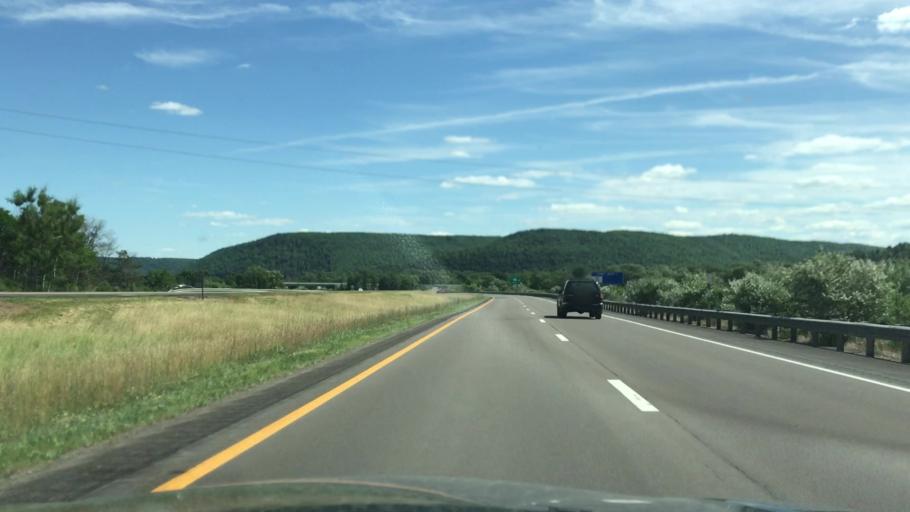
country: US
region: New York
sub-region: Steuben County
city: Bath
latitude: 42.4071
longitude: -77.4094
